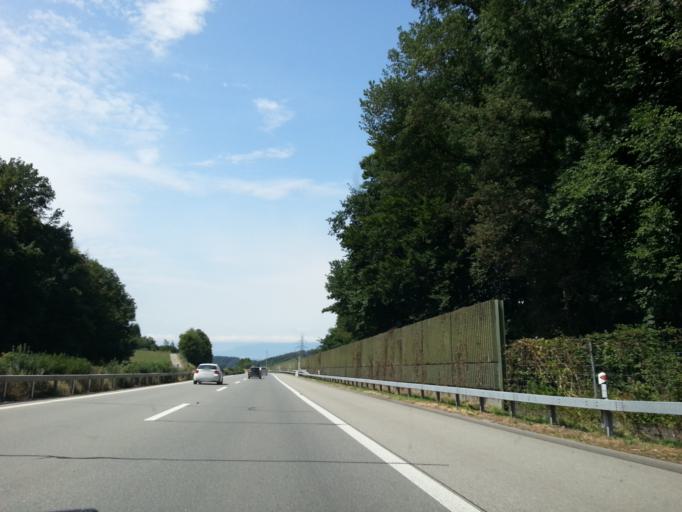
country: CH
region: Bern
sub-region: Bern-Mittelland District
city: Muhleberg
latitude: 46.9594
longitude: 7.2864
